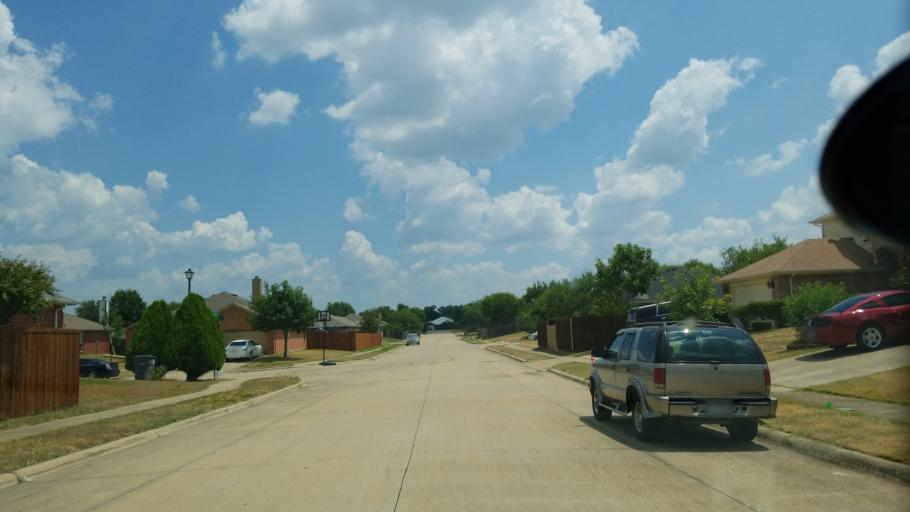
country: US
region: Texas
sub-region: Dallas County
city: Duncanville
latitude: 32.6794
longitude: -96.8988
